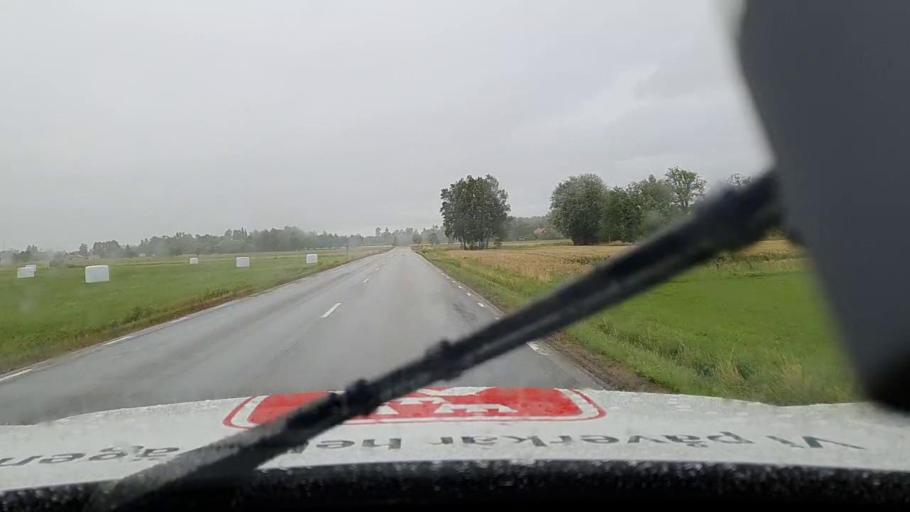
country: SE
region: Vaestra Goetaland
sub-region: Toreboda Kommun
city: Toereboda
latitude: 58.6943
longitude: 14.1311
